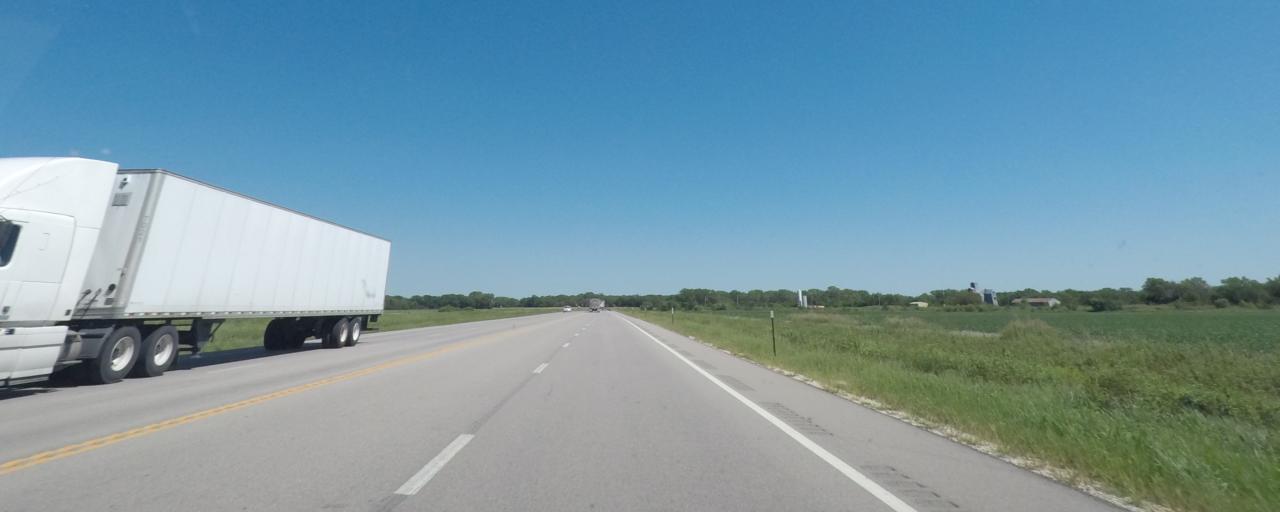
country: US
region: Kansas
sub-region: Chase County
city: Cottonwood Falls
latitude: 38.4049
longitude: -96.3992
